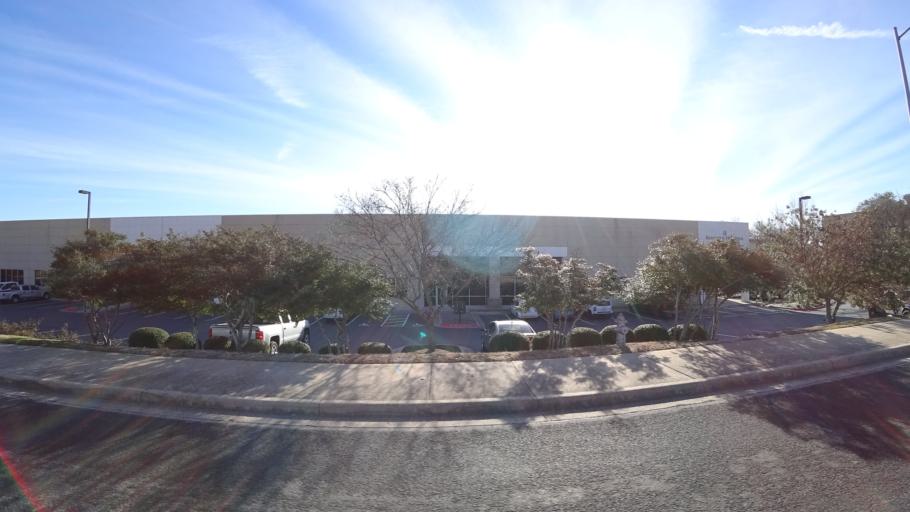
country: US
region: Texas
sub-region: Travis County
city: Wells Branch
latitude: 30.3993
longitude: -97.7090
